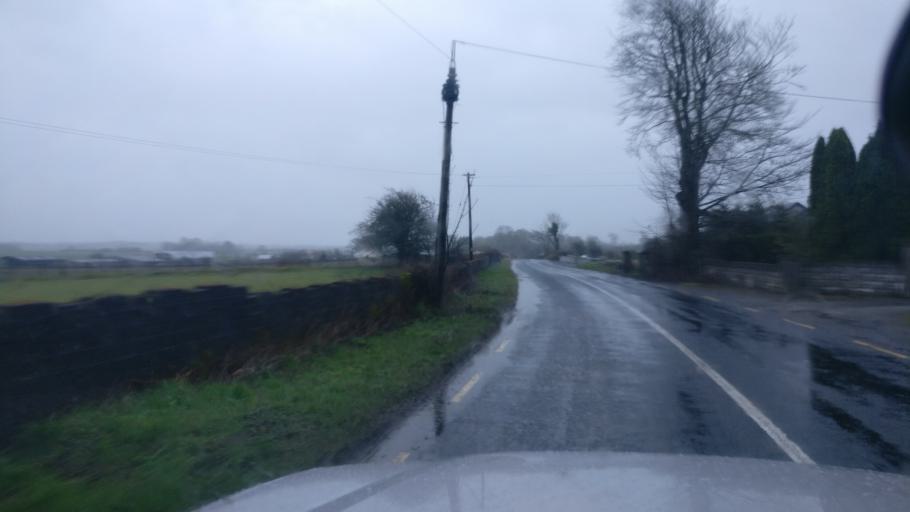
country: IE
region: Connaught
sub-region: County Galway
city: Ballinasloe
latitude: 53.2802
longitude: -8.2228
